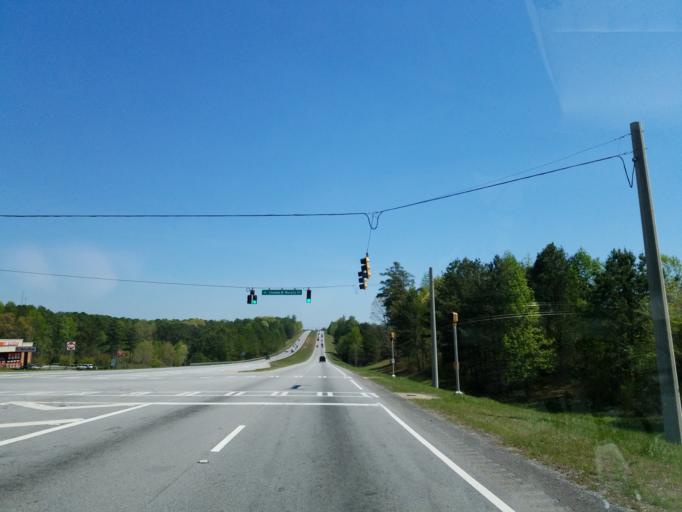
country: US
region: Georgia
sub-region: Paulding County
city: Dallas
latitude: 33.9081
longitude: -84.8210
